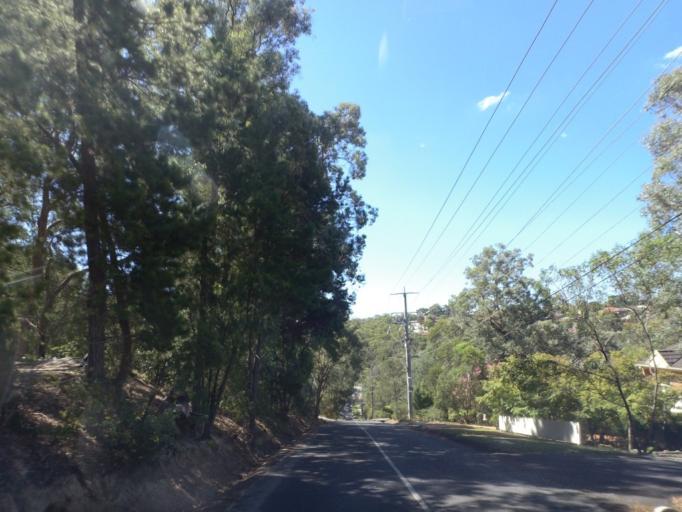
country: AU
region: Victoria
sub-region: Manningham
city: Park Orchards
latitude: -37.7970
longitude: 145.2162
